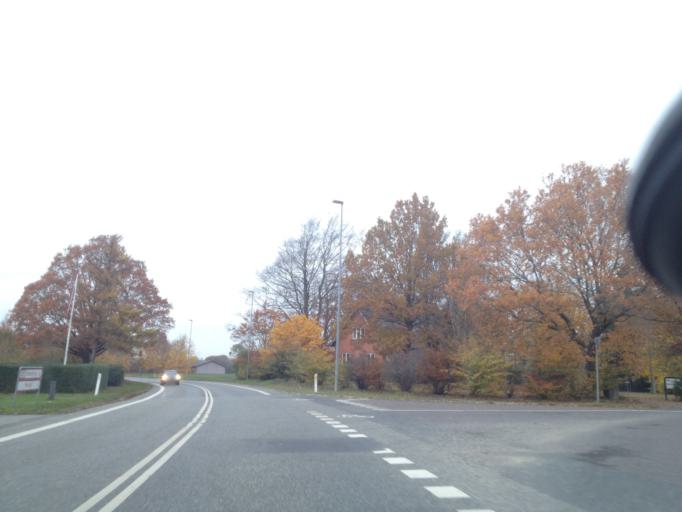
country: DK
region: South Denmark
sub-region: Nordfyns Kommune
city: Sonderso
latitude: 55.4272
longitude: 10.2541
